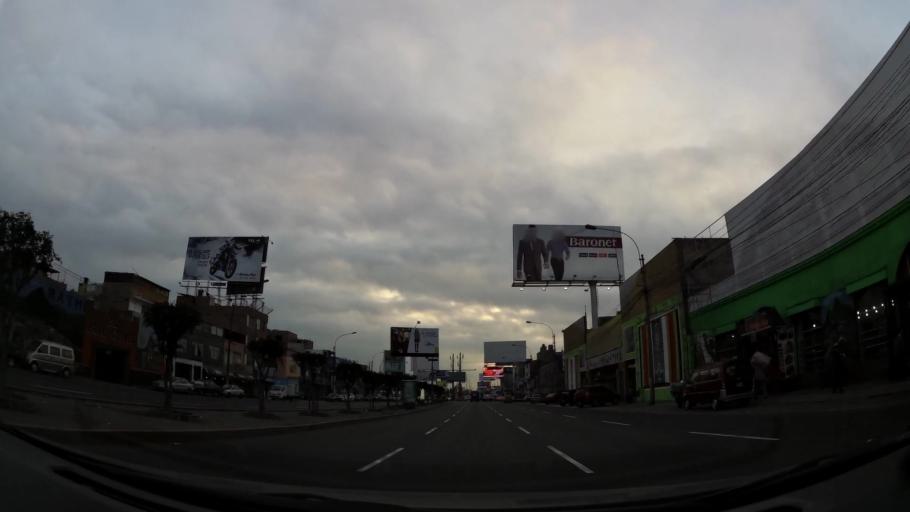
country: PE
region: Lima
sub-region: Lima
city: San Isidro
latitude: -12.0824
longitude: -77.0689
